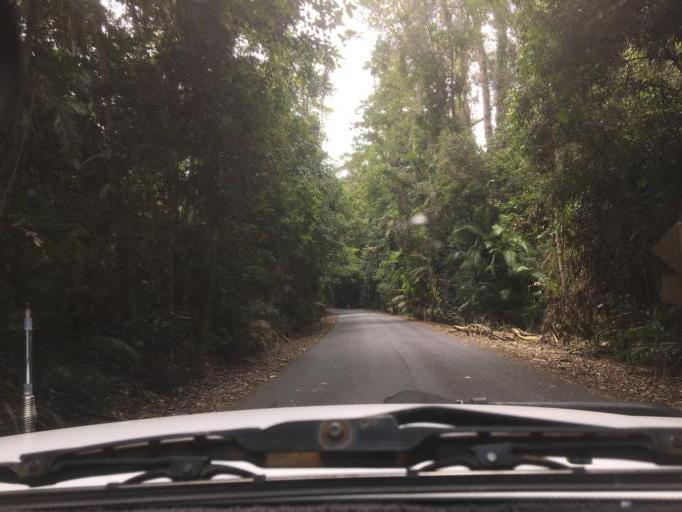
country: AU
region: Queensland
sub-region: Tablelands
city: Tolga
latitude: -17.2812
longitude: 145.6282
